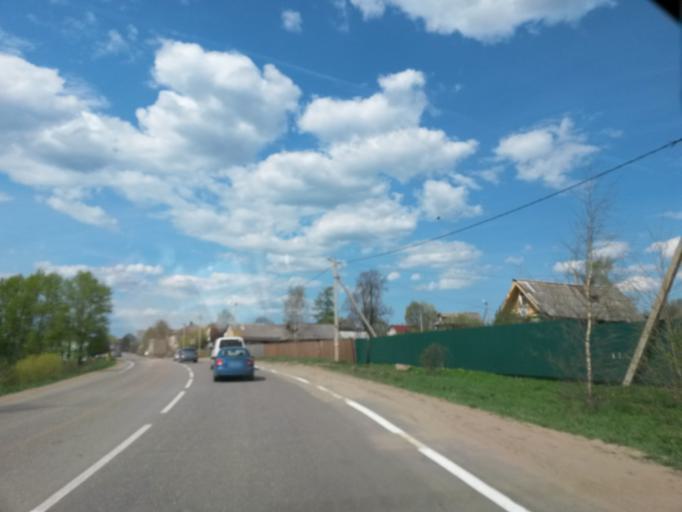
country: RU
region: Jaroslavl
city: Bol'shoye Selo
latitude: 57.7226
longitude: 38.9384
